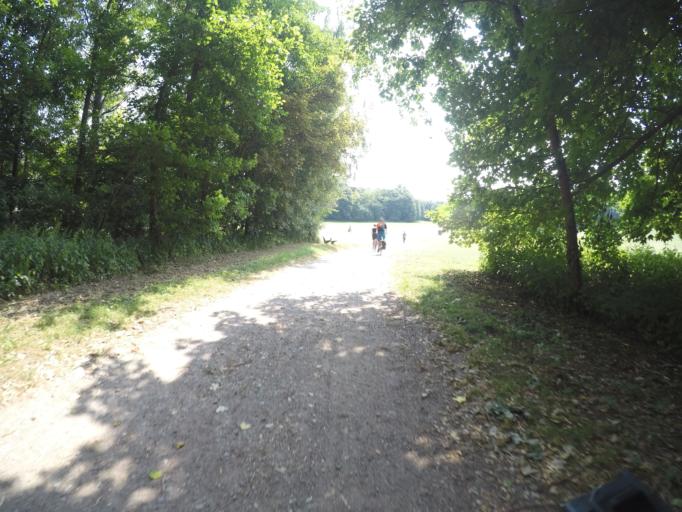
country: DE
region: Schleswig-Holstein
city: Oststeinbek
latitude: 53.5579
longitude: 10.1461
